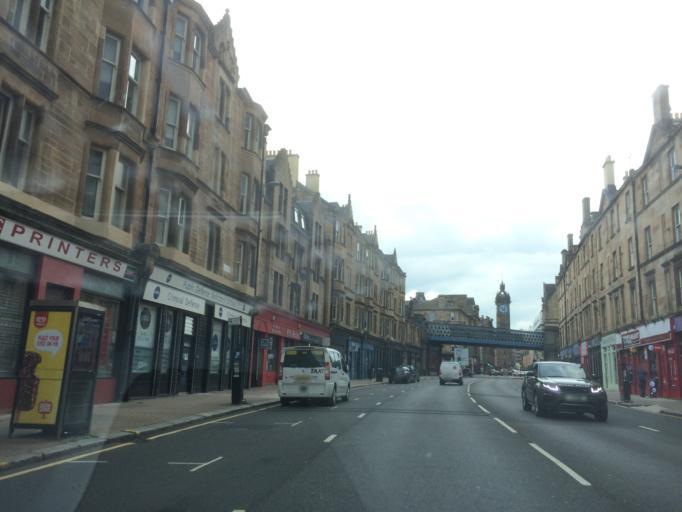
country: GB
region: Scotland
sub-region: Glasgow City
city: Glasgow
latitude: 55.8549
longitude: -4.2455
